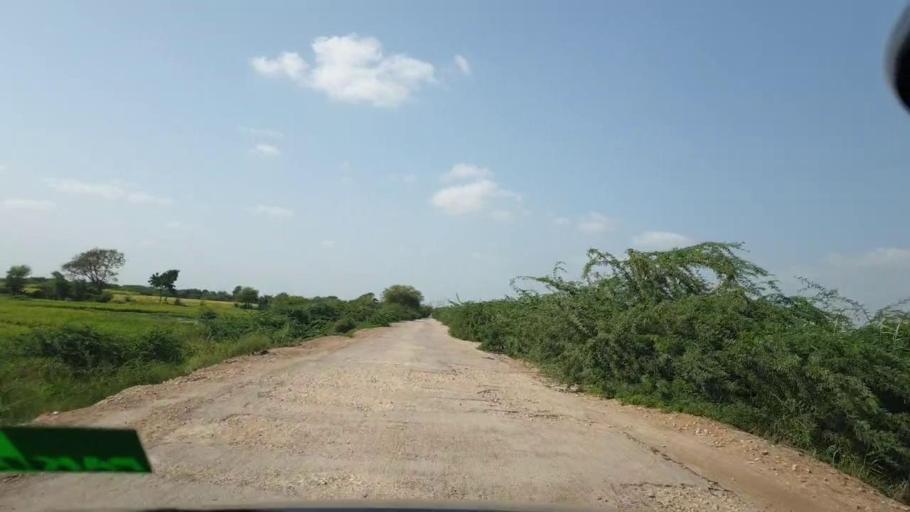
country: PK
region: Sindh
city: Tando Bago
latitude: 24.6684
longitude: 69.1958
